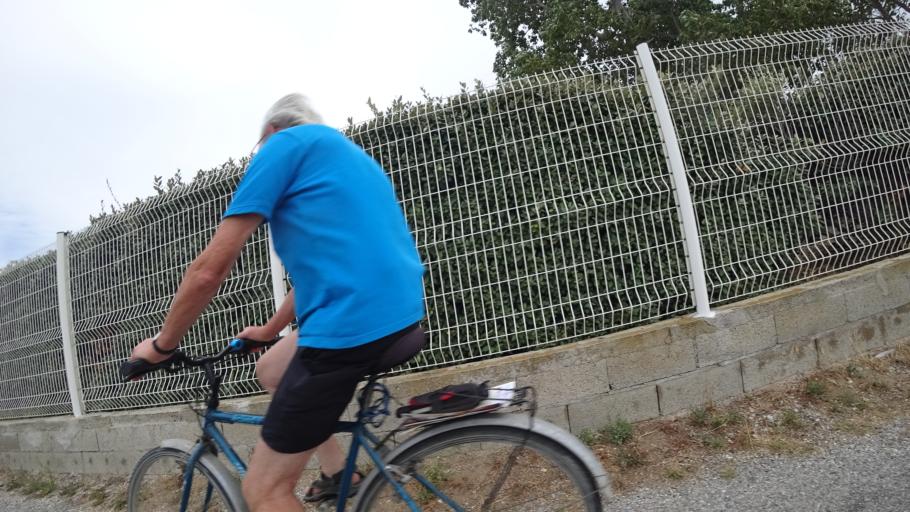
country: FR
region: Languedoc-Roussillon
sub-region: Departement des Pyrenees-Orientales
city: Le Barcares
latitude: 42.8046
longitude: 3.0330
